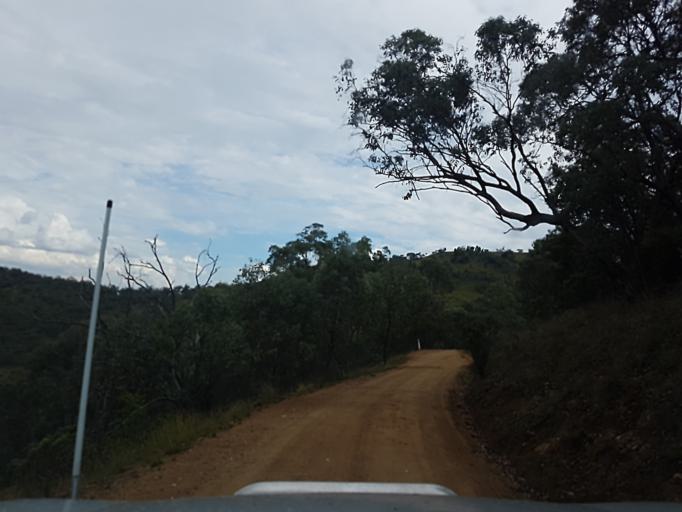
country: AU
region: New South Wales
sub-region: Snowy River
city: Jindabyne
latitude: -36.9447
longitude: 148.3478
